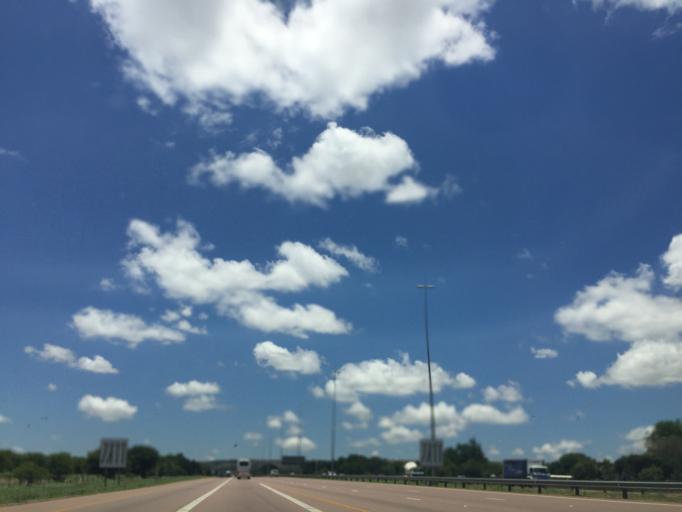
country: ZA
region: Gauteng
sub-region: City of Tshwane Metropolitan Municipality
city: Pretoria
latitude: -25.6537
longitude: 28.2744
